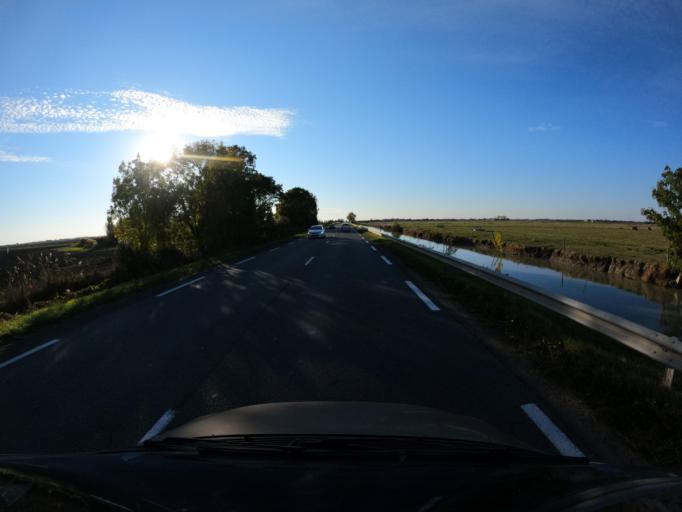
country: FR
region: Pays de la Loire
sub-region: Departement de la Vendee
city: Chaille-les-Marais
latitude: 46.4128
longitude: -1.0506
